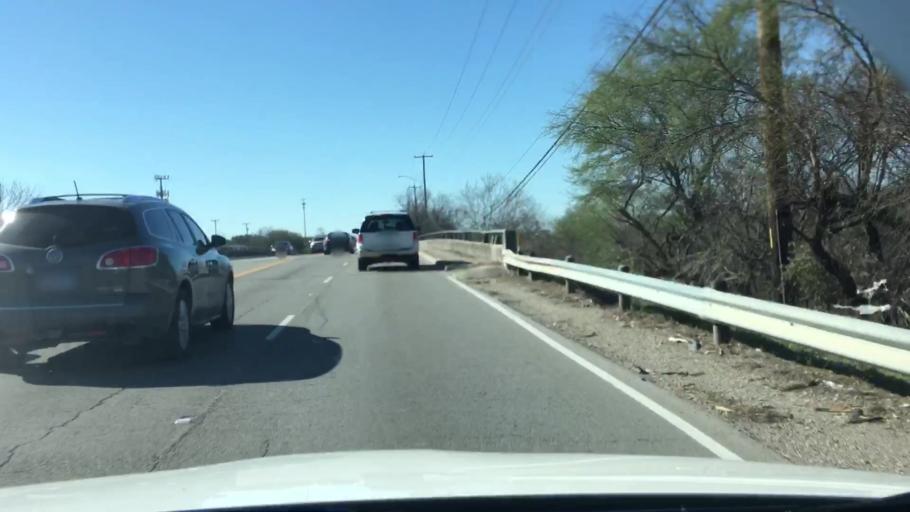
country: US
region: Texas
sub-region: Bexar County
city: Alamo Heights
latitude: 29.5426
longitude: -98.4414
